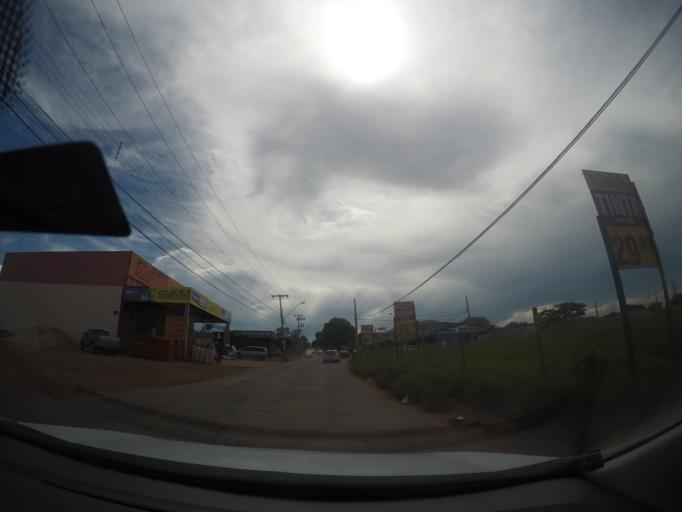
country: BR
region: Goias
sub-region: Trindade
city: Trindade
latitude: -16.6844
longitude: -49.3794
